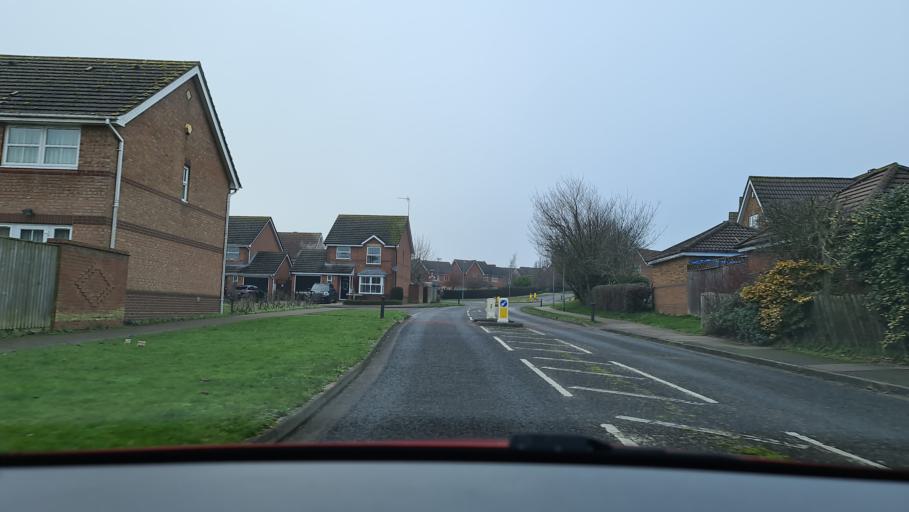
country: GB
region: England
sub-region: Northamptonshire
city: Brackley
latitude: 52.0357
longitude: -1.1585
